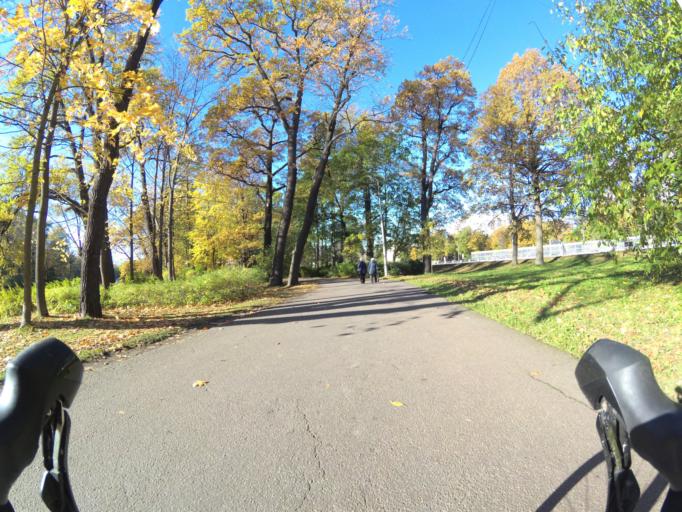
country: RU
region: Leningrad
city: Krestovskiy ostrov
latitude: 59.9818
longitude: 30.2585
